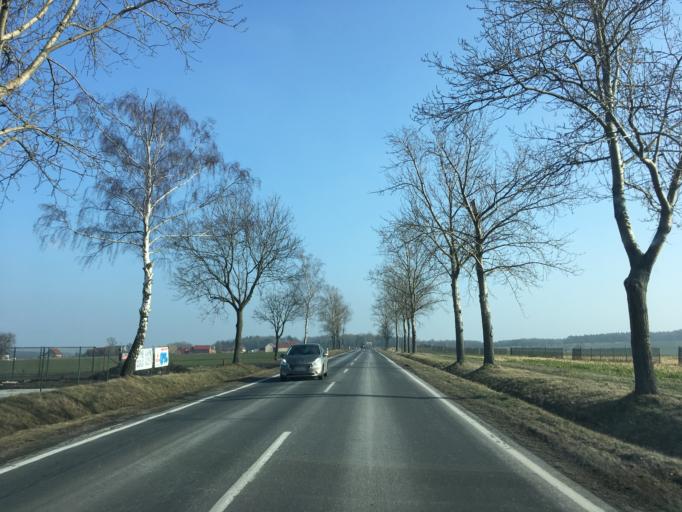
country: PL
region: Lower Silesian Voivodeship
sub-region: Powiat zlotoryjski
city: Olszanica
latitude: 51.2777
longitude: 15.8335
